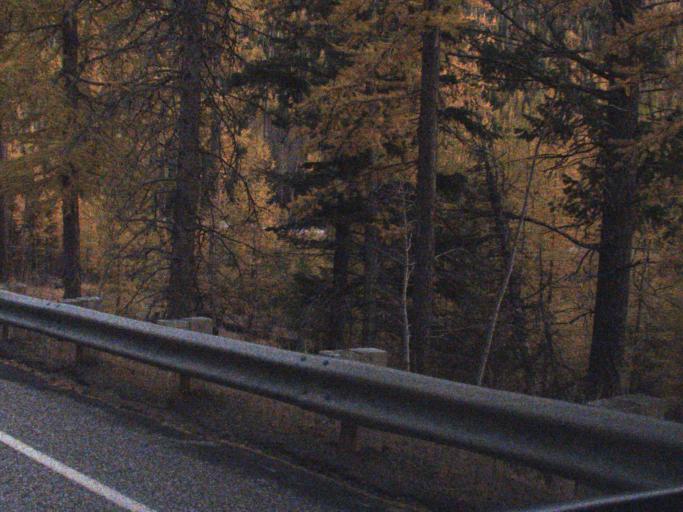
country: US
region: Washington
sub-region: Ferry County
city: Republic
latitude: 48.5982
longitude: -118.5118
